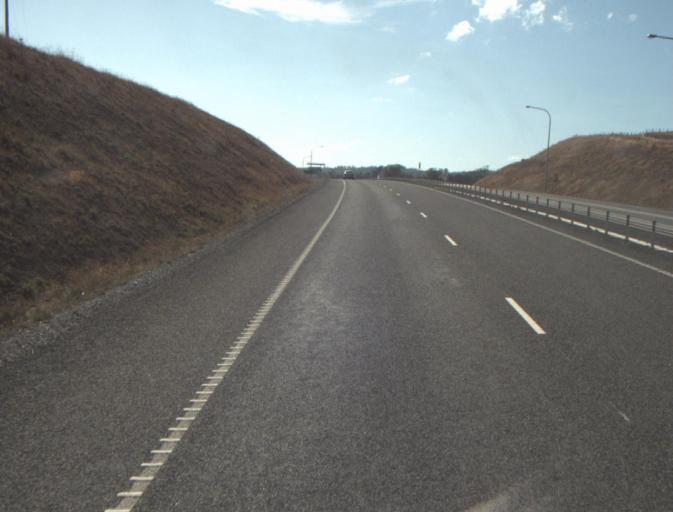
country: AU
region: Tasmania
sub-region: Launceston
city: Mayfield
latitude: -41.3574
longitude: 147.1055
